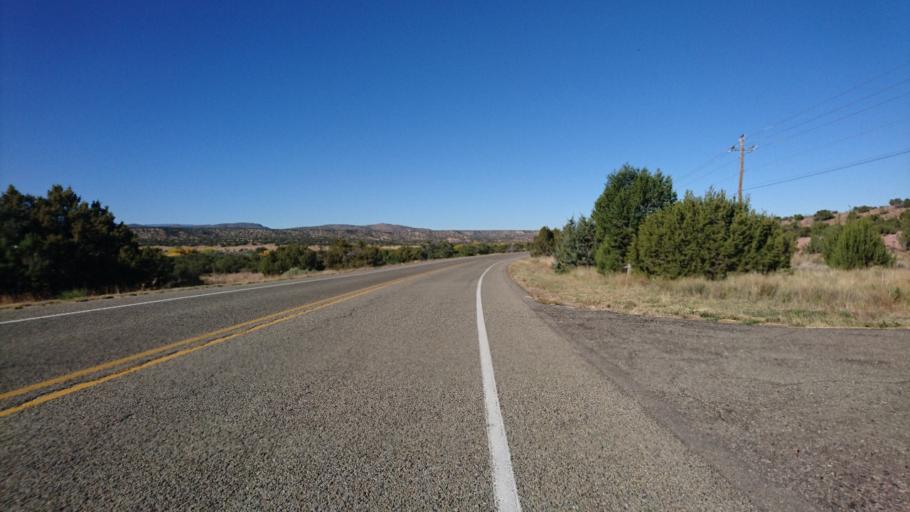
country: US
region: New Mexico
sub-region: Santa Fe County
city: La Cienega
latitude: 35.4296
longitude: -106.0916
